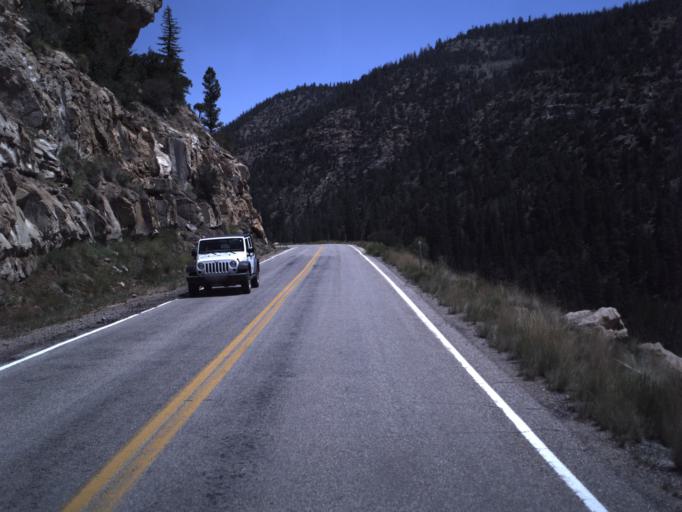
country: US
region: Utah
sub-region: Emery County
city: Orangeville
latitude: 39.2891
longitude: -111.2678
